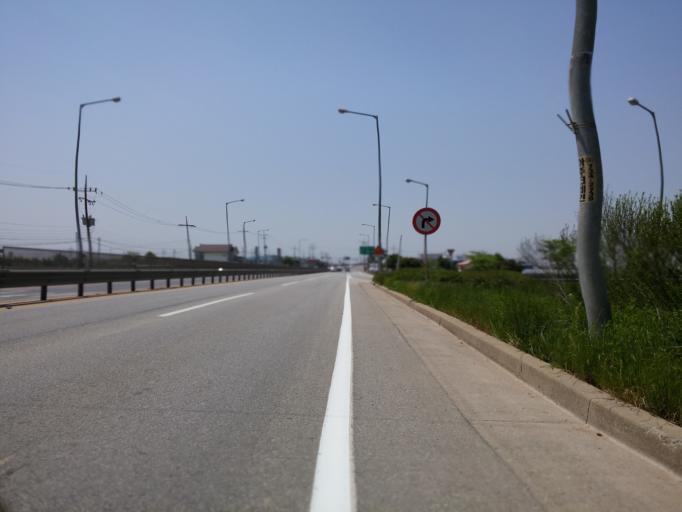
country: KR
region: Chungcheongnam-do
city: Nonsan
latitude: 36.2127
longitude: 127.1190
